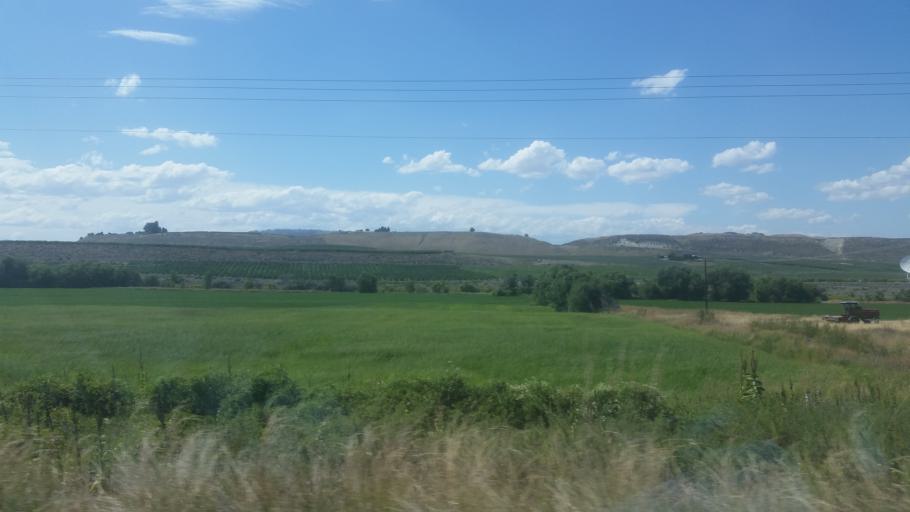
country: US
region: Washington
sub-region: Okanogan County
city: Brewster
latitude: 48.1252
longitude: -119.6738
